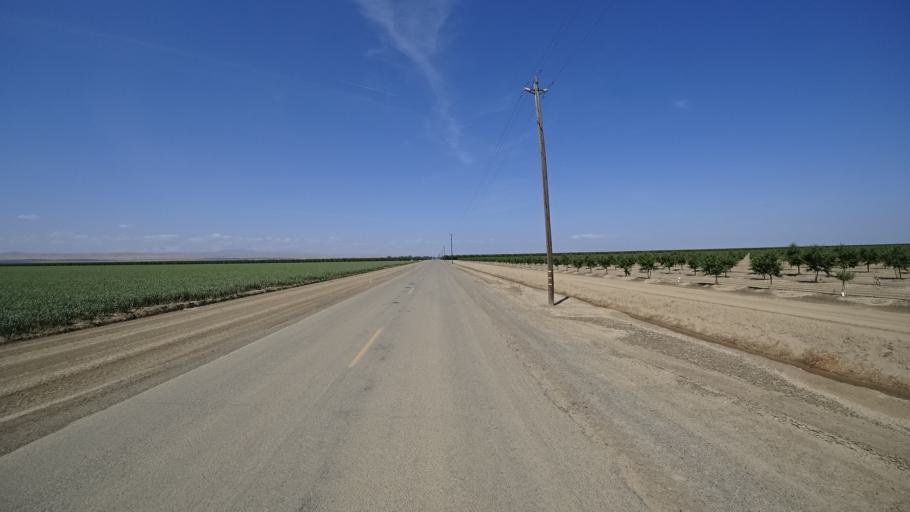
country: US
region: California
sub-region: Kings County
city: Kettleman City
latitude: 36.0943
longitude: -119.9819
